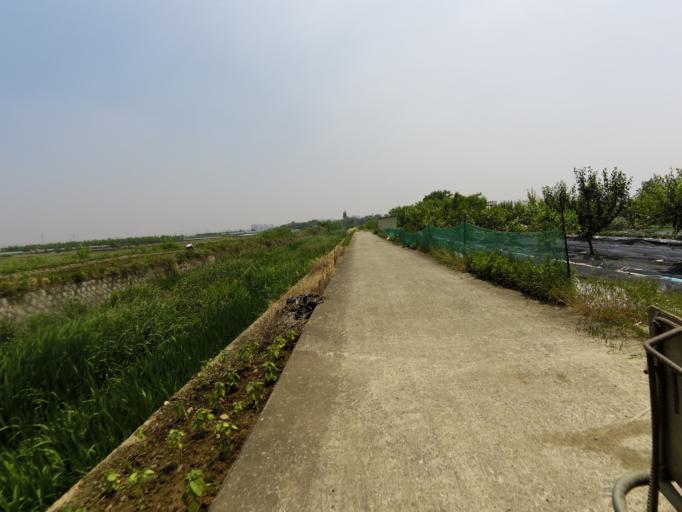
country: KR
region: Gyeongsangbuk-do
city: Gyeongsan-si
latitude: 35.8458
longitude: 128.7366
